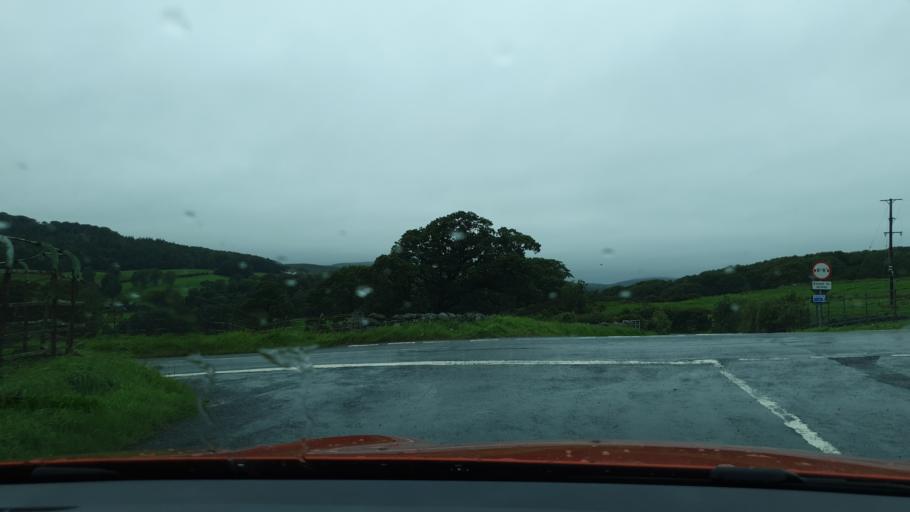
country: GB
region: England
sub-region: Cumbria
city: Ulverston
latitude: 54.2507
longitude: -3.0563
